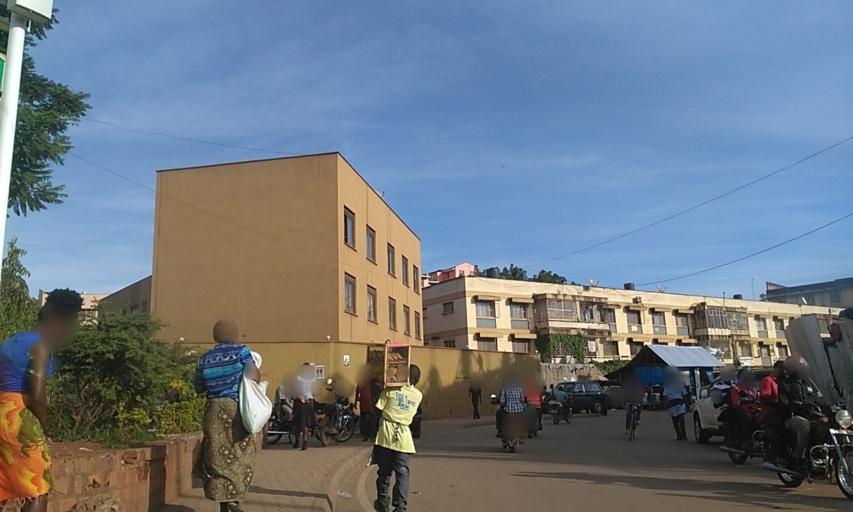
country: UG
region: Central Region
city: Kampala Central Division
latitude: 0.3217
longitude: 32.5718
